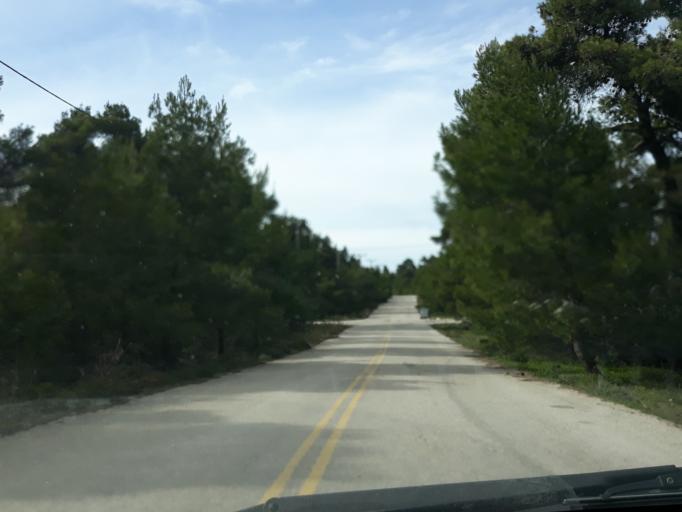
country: GR
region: Attica
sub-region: Nomarchia Anatolikis Attikis
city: Afidnes
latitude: 38.2126
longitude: 23.7973
